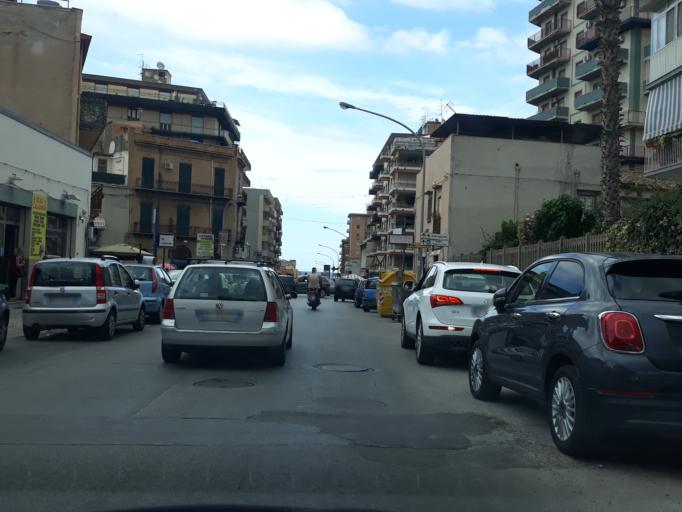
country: IT
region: Sicily
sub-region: Palermo
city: Ciaculli
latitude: 38.0984
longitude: 13.3913
